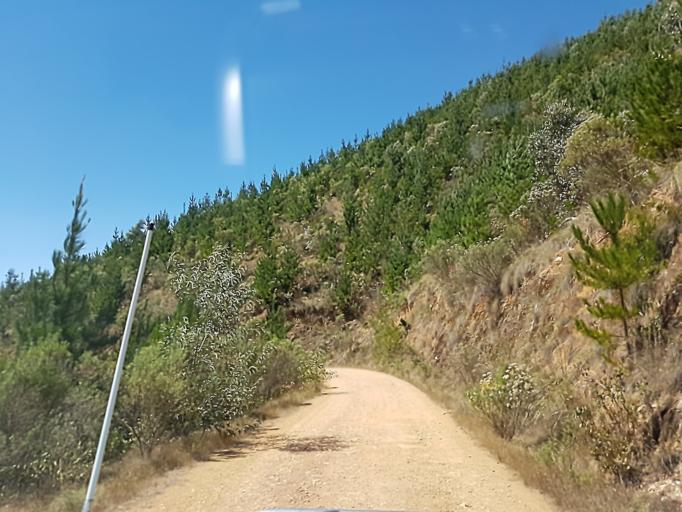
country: AU
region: Victoria
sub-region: Alpine
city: Mount Beauty
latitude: -36.7429
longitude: 146.9594
